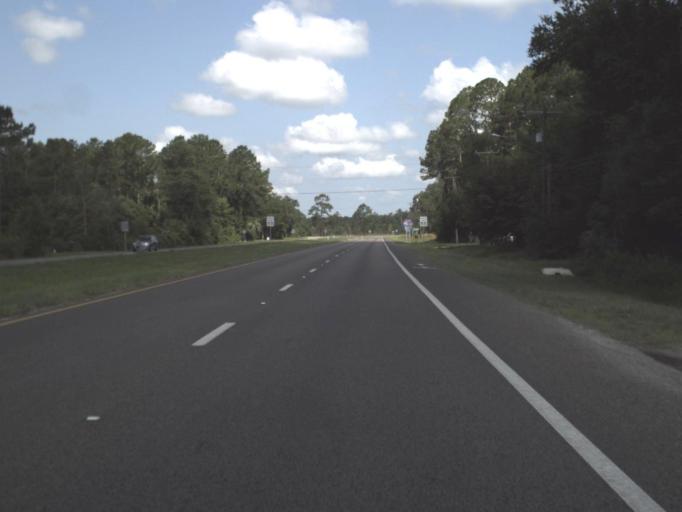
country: US
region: Florida
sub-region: Alachua County
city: Gainesville
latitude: 29.5128
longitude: -82.2861
